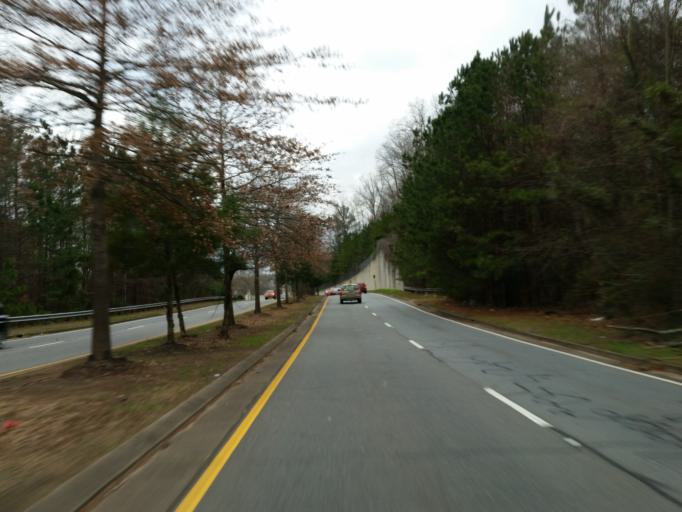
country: US
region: Georgia
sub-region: Cherokee County
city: Woodstock
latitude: 34.0336
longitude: -84.5307
